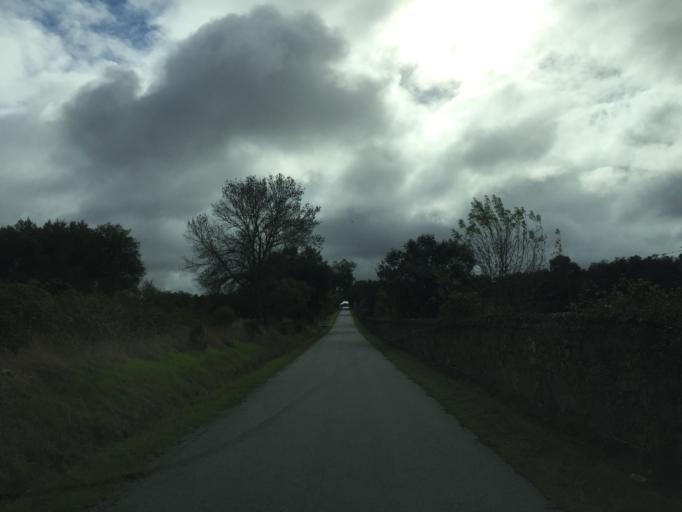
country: PT
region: Portalegre
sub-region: Alter do Chao
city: Alter do Chao
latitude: 39.2292
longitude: -7.6822
